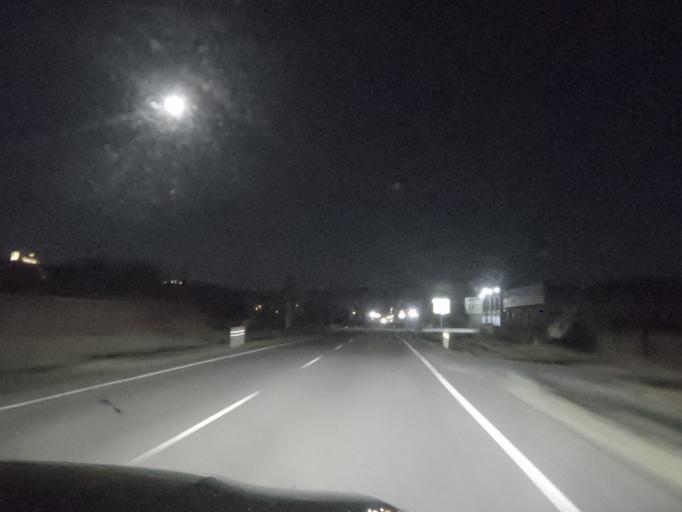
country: ES
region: Galicia
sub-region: Provincia de Ourense
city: Verin
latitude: 41.9431
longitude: -7.4708
